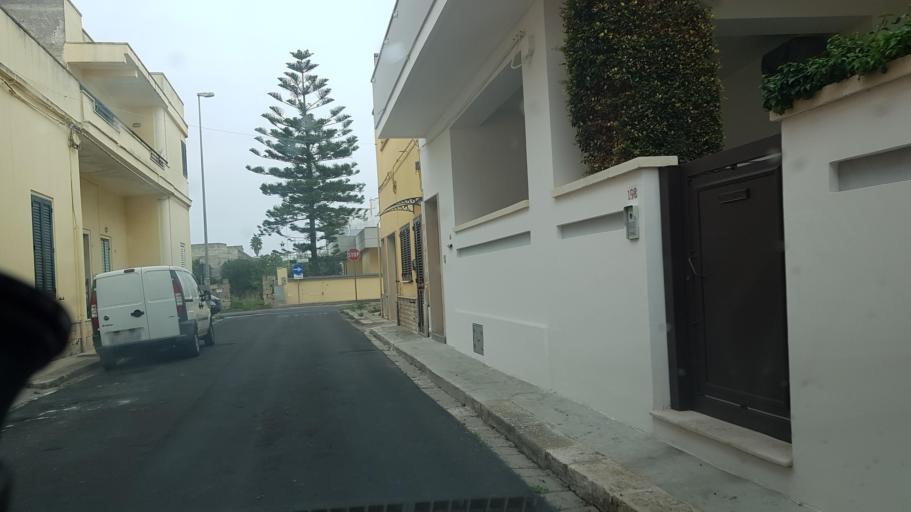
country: IT
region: Apulia
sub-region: Provincia di Lecce
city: Leverano
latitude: 40.2936
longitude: 18.0016
